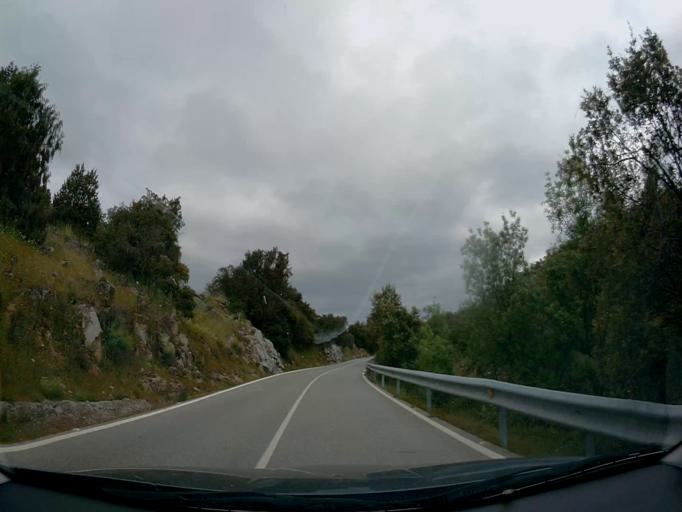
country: ES
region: Madrid
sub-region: Provincia de Madrid
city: Navalagamella
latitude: 40.4457
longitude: -4.1159
